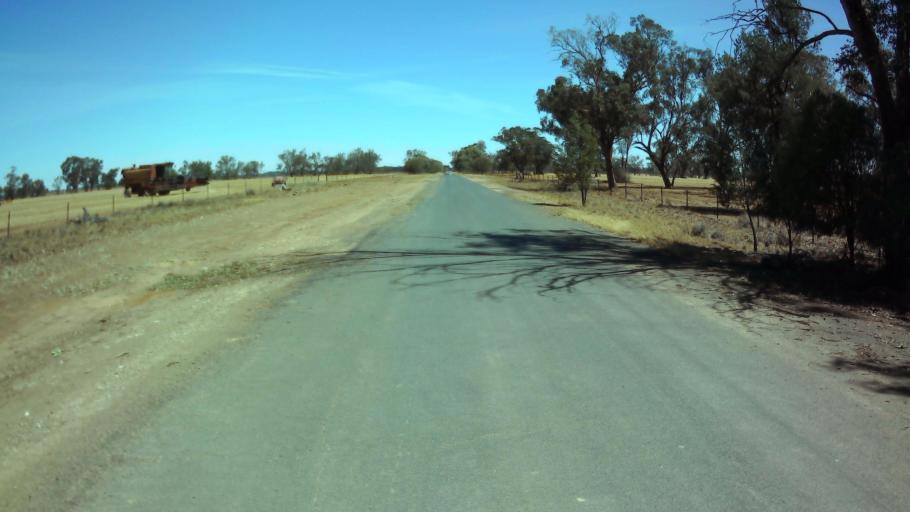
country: AU
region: New South Wales
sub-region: Weddin
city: Grenfell
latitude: -33.8449
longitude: 147.6966
